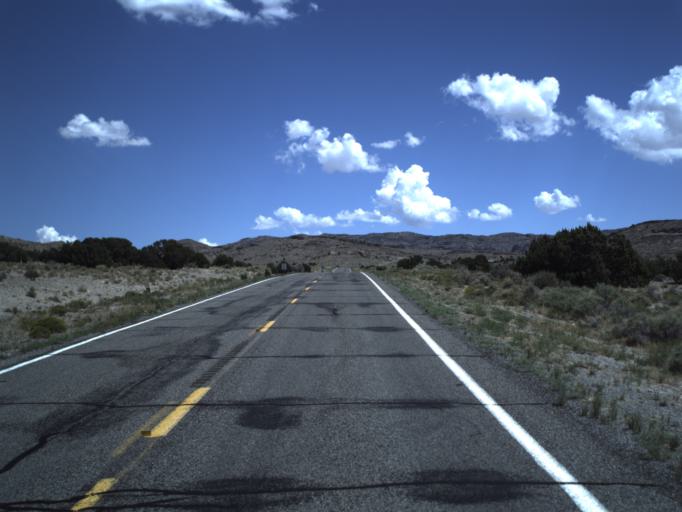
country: US
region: Utah
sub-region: Beaver County
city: Milford
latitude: 39.0762
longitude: -113.7115
